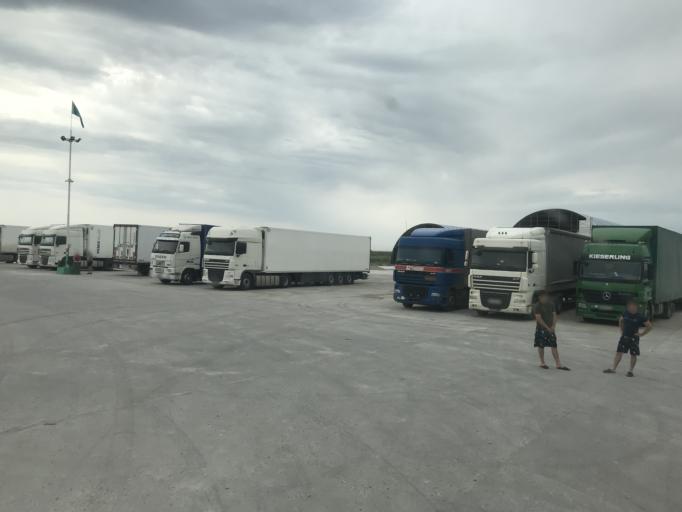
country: KZ
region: Ongtustik Qazaqstan
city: Asykata
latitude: 40.9623
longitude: 68.4611
